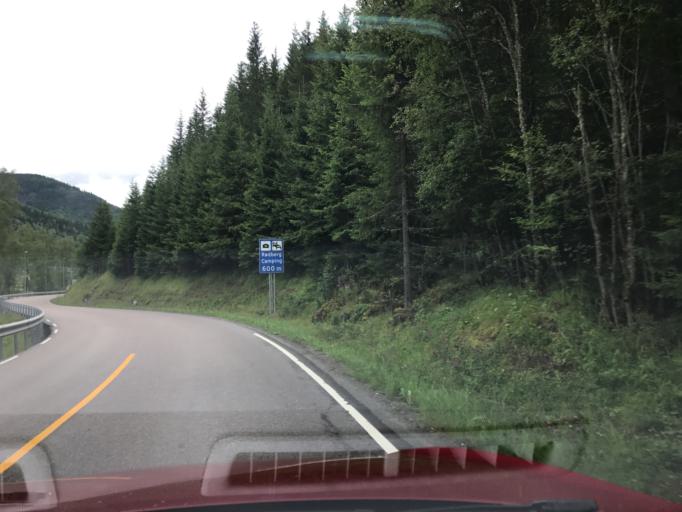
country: NO
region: Buskerud
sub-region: Nore og Uvdal
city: Rodberg
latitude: 60.2658
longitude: 8.9496
